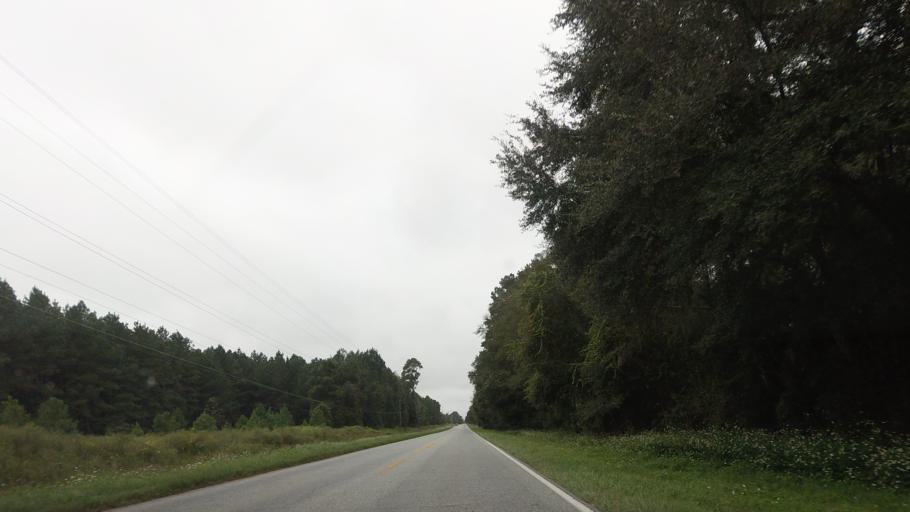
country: US
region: Georgia
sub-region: Lowndes County
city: Valdosta
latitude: 30.8143
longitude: -83.2451
